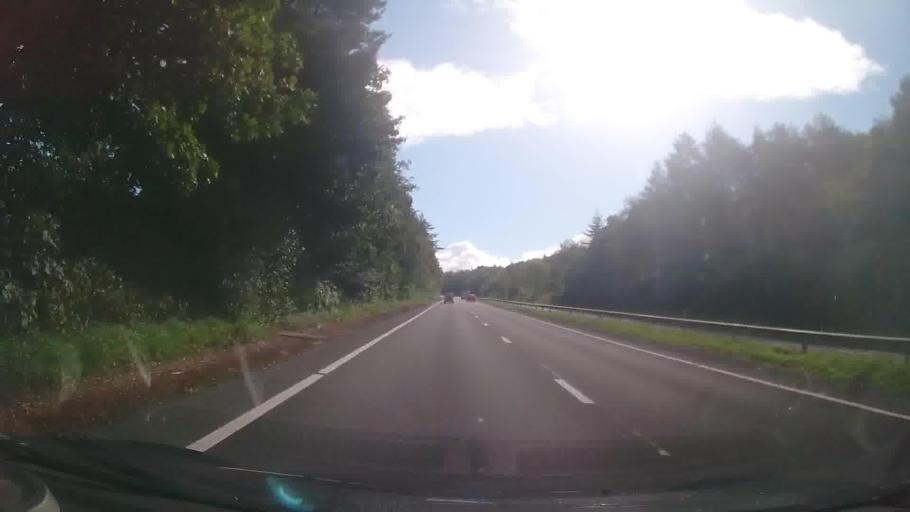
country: GB
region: Wales
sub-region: Carmarthenshire
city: Carmarthen
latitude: 51.8424
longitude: -4.2512
